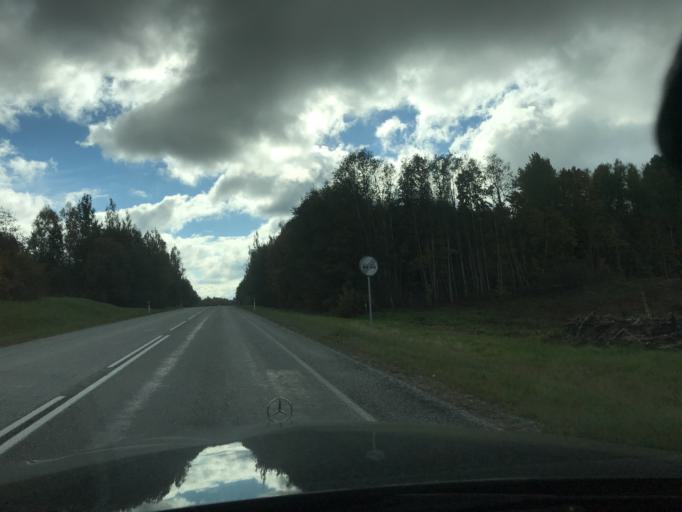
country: RU
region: Pskov
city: Pechory
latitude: 57.7005
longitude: 27.3252
